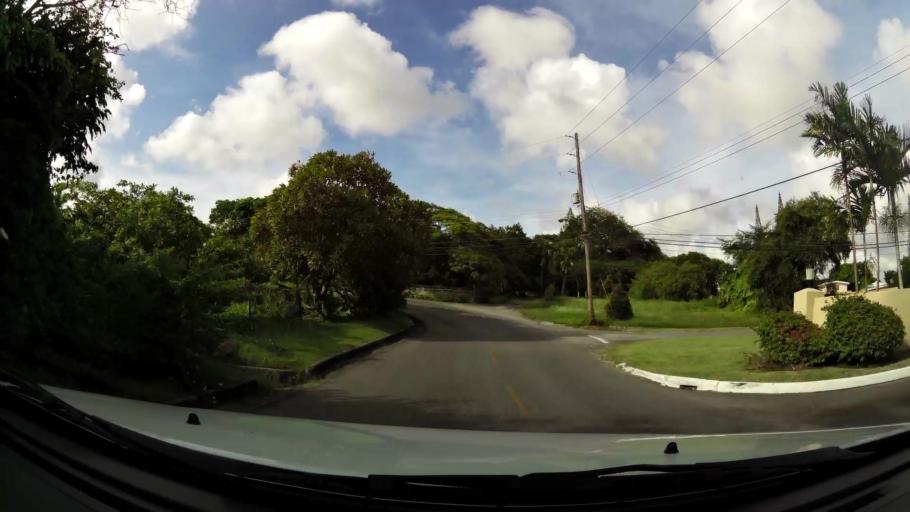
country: BB
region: Saint Michael
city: Bridgetown
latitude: 13.0758
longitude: -59.5836
